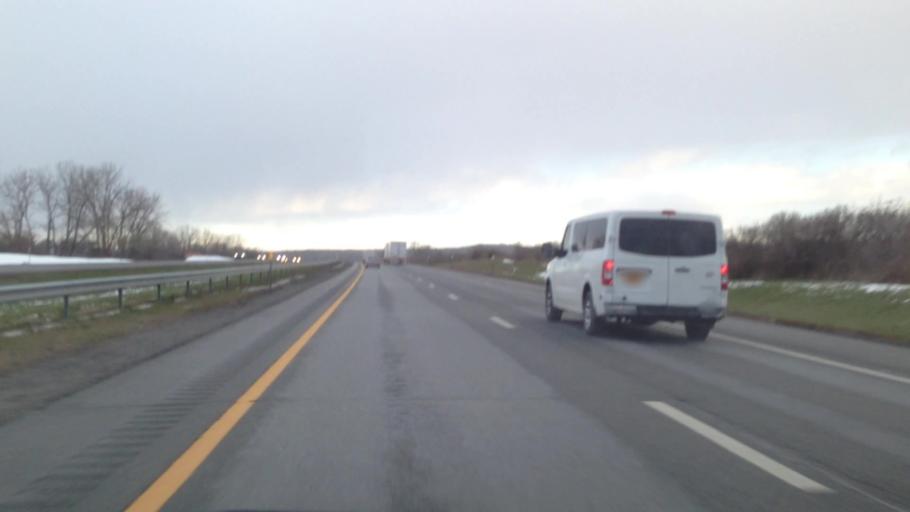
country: US
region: New York
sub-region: Montgomery County
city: Saint Johnsville
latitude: 42.9824
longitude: -74.6594
